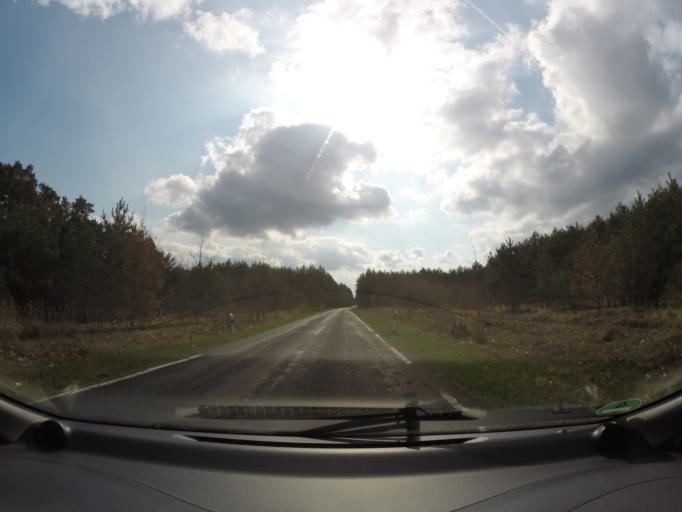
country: DE
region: Brandenburg
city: Spreenhagen
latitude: 52.4274
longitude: 13.9428
